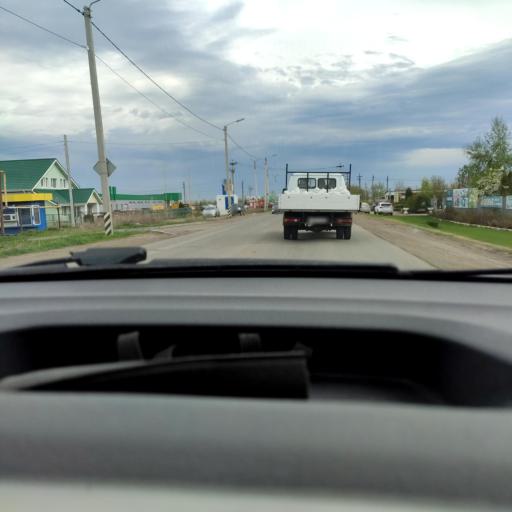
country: RU
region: Samara
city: Podstepki
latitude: 53.5212
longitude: 49.1916
